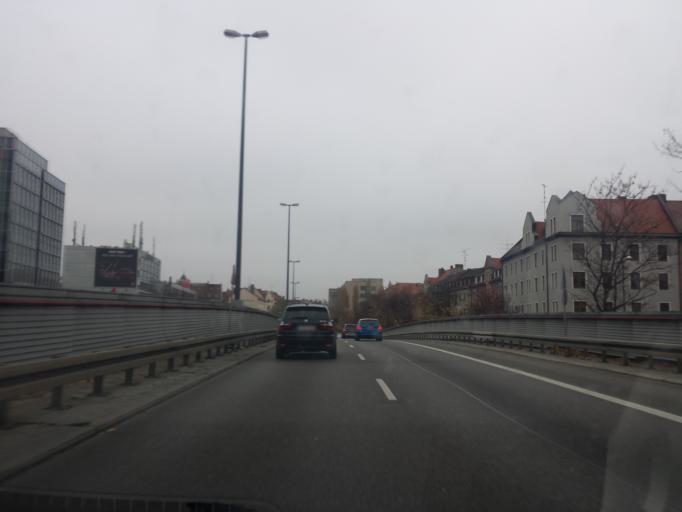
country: DE
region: Bavaria
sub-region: Upper Bavaria
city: Munich
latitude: 48.1405
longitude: 11.5343
